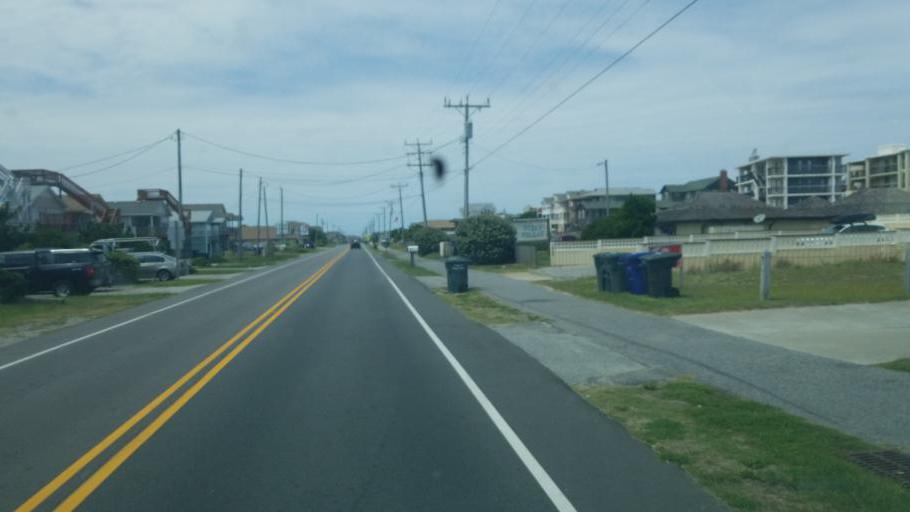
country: US
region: North Carolina
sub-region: Dare County
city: Nags Head
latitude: 35.9132
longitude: -75.5993
